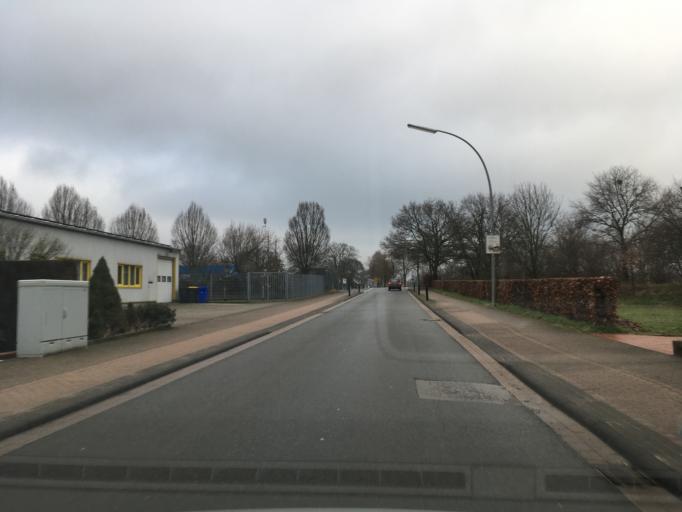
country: NL
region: Overijssel
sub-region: Gemeente Enschede
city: Enschede
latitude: 52.1338
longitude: 6.9162
